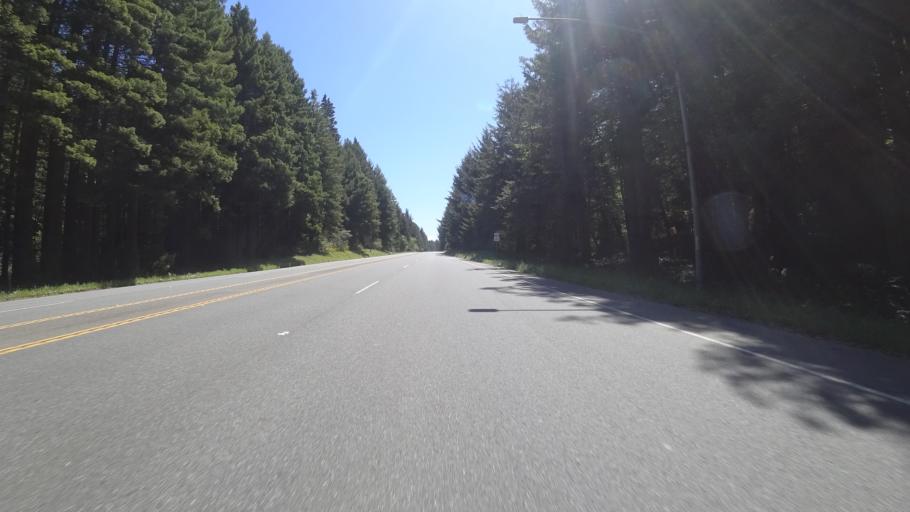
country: US
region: California
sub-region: Humboldt County
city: Westhaven-Moonstone
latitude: 41.0610
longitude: -124.1373
